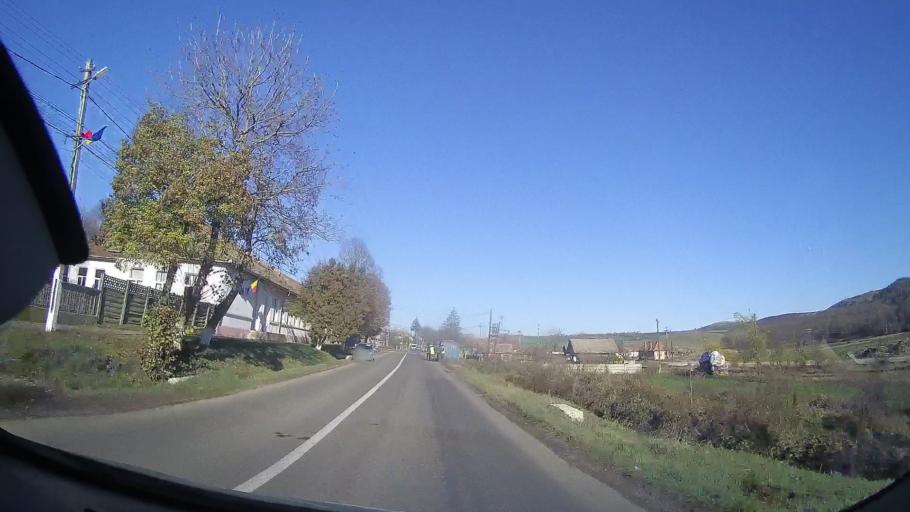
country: RO
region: Mures
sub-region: Comuna Sarmasu
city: Balda
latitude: 46.7315
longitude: 24.1464
